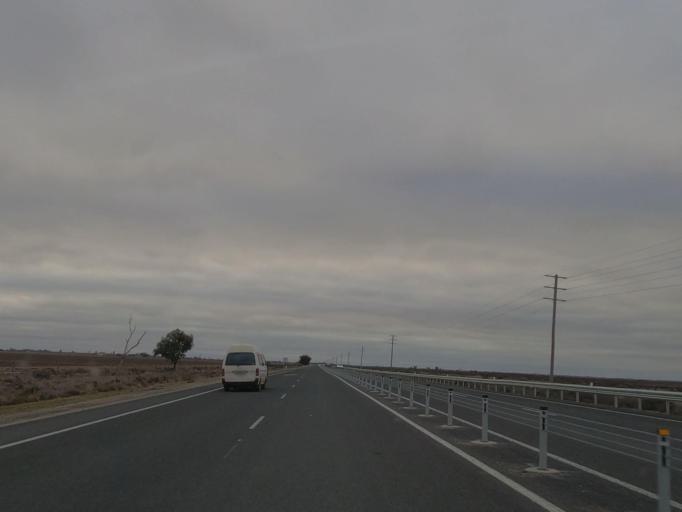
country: AU
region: Victoria
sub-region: Swan Hill
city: Swan Hill
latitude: -35.5087
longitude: 143.7228
